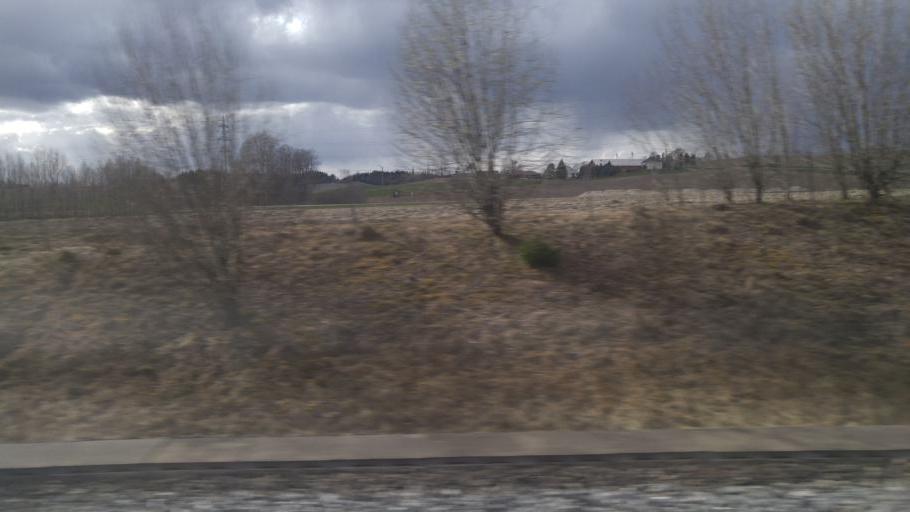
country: NO
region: Akershus
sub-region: Skedsmo
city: Leirsund
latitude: 59.9904
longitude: 11.0793
